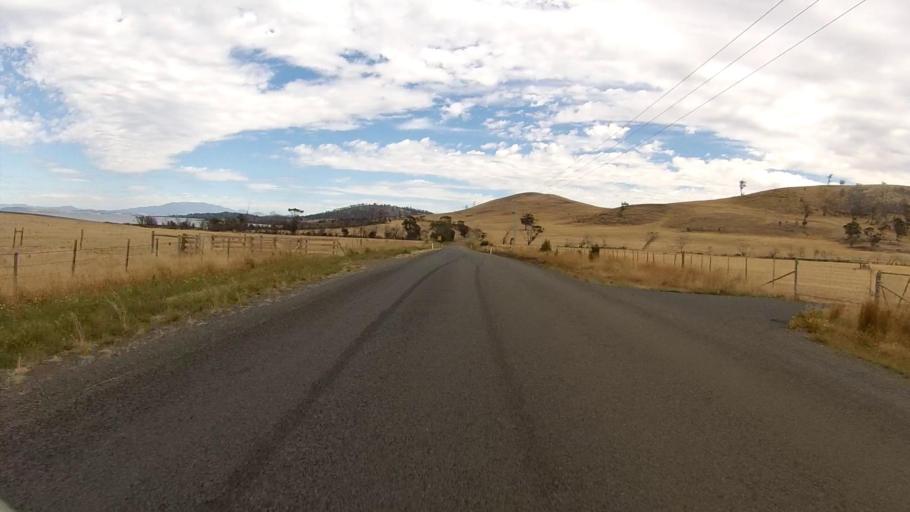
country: AU
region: Tasmania
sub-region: Sorell
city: Sorell
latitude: -42.8984
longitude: 147.7575
